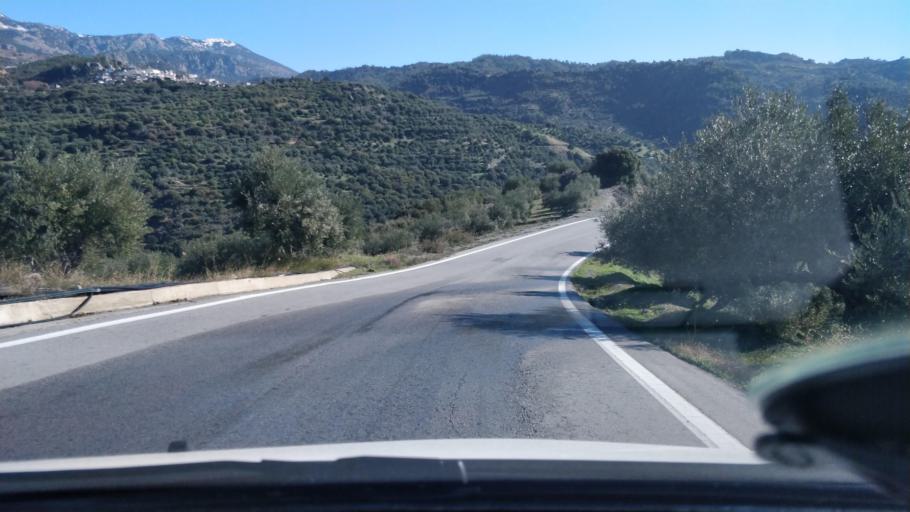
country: GR
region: Crete
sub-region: Nomos Irakleiou
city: Kastelli
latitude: 35.0317
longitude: 25.4471
